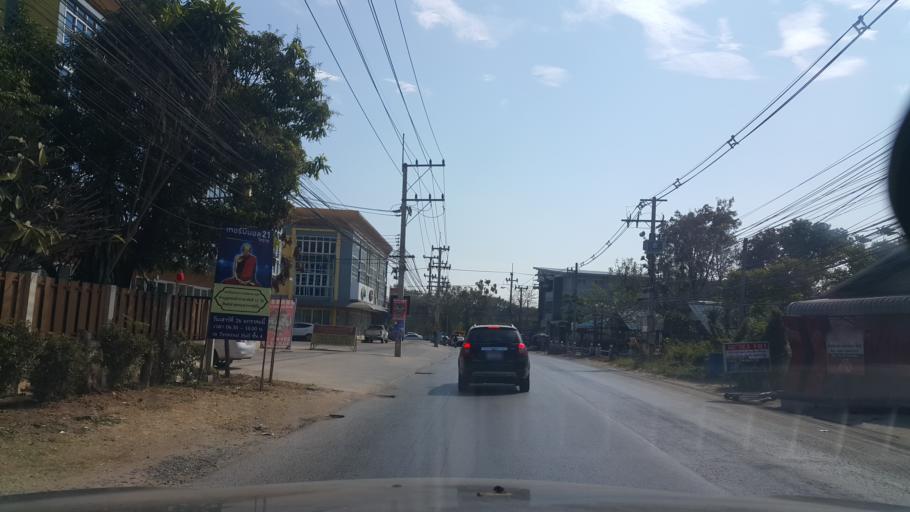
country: TH
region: Nakhon Ratchasima
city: Nakhon Ratchasima
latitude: 14.9475
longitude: 102.0525
